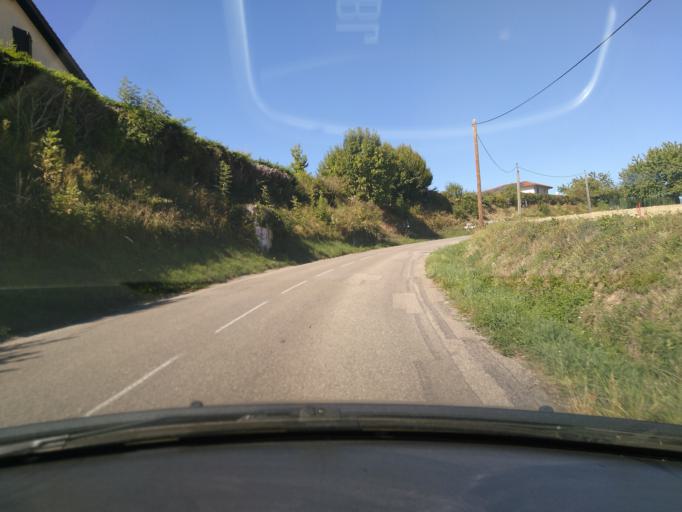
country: FR
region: Rhone-Alpes
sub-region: Departement de l'Isere
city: La Murette
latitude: 45.3716
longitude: 5.5257
